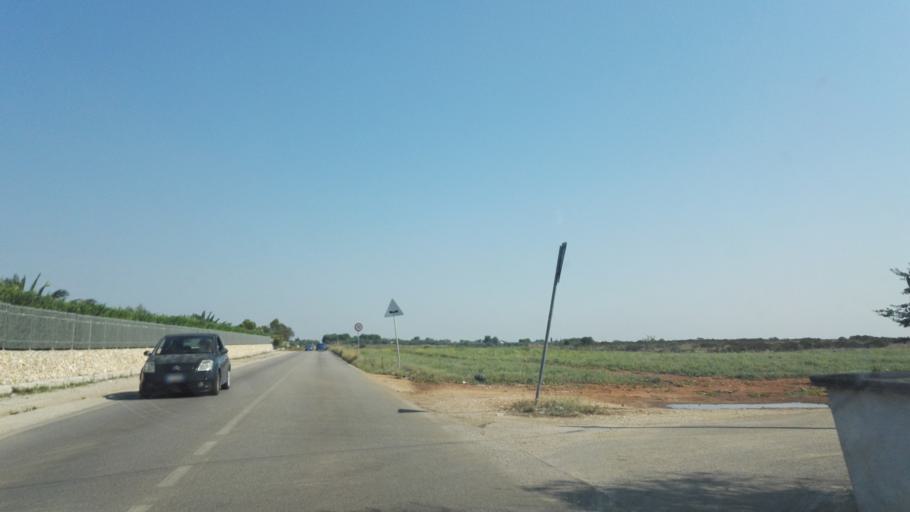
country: IT
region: Apulia
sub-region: Provincia di Lecce
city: Nardo
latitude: 40.1308
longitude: 18.0193
